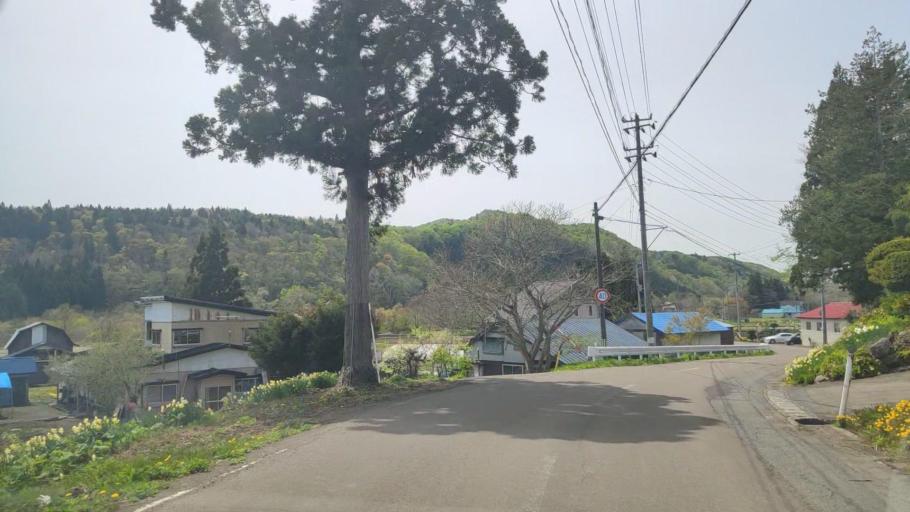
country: JP
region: Aomori
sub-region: Misawa Shi
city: Inuotose
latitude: 40.7892
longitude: 141.1072
